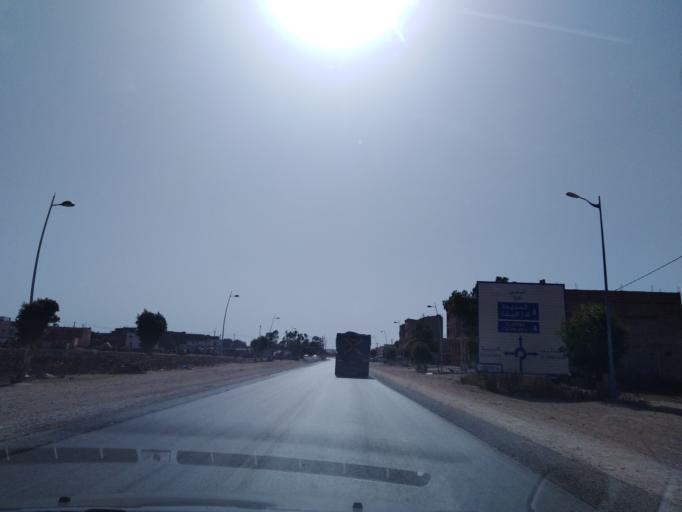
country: MA
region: Doukkala-Abda
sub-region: Safi
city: Safi
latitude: 32.2536
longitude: -8.9784
